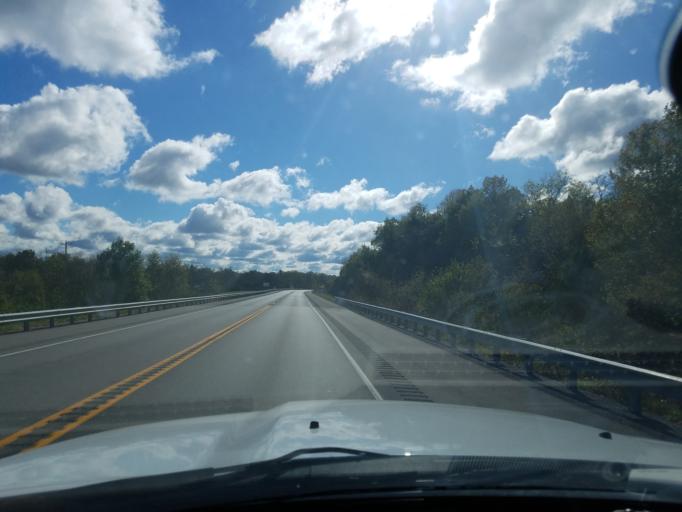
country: US
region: Kentucky
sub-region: Lincoln County
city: Stanford
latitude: 37.5377
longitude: -84.6465
